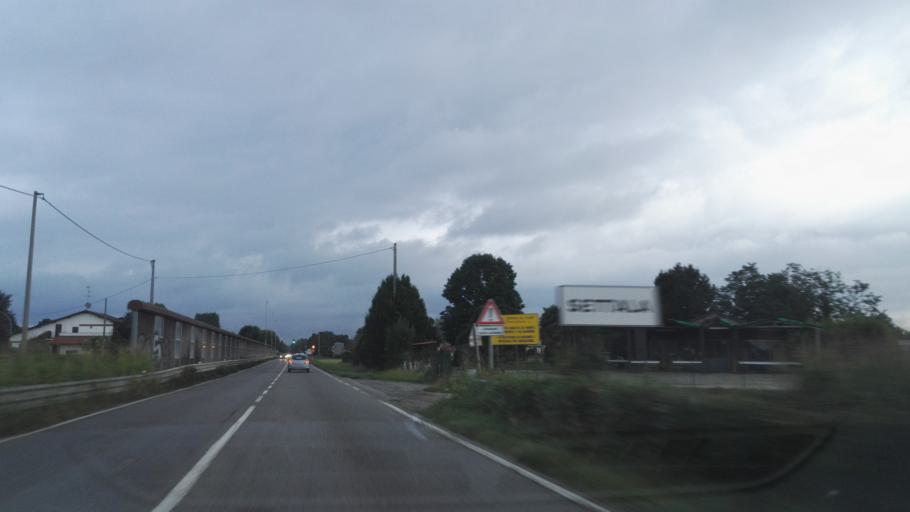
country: IT
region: Lombardy
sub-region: Citta metropolitana di Milano
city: Settala
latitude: 45.4499
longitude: 9.3936
